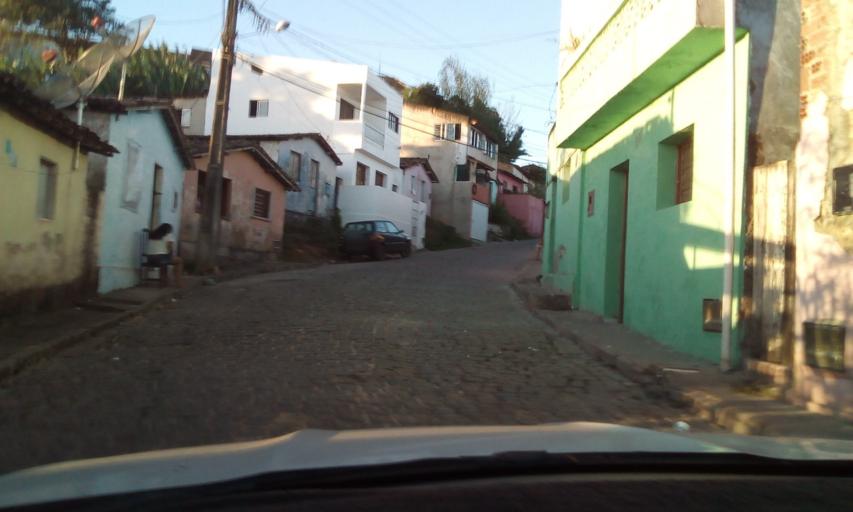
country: BR
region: Paraiba
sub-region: Areia
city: Areia
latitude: -6.9716
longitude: -35.7051
